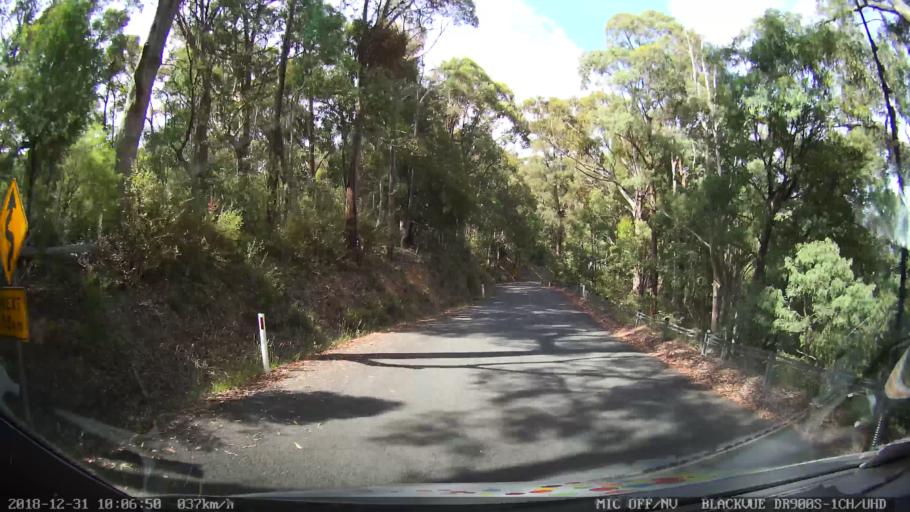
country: AU
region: New South Wales
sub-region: Snowy River
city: Jindabyne
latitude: -36.5306
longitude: 148.1871
